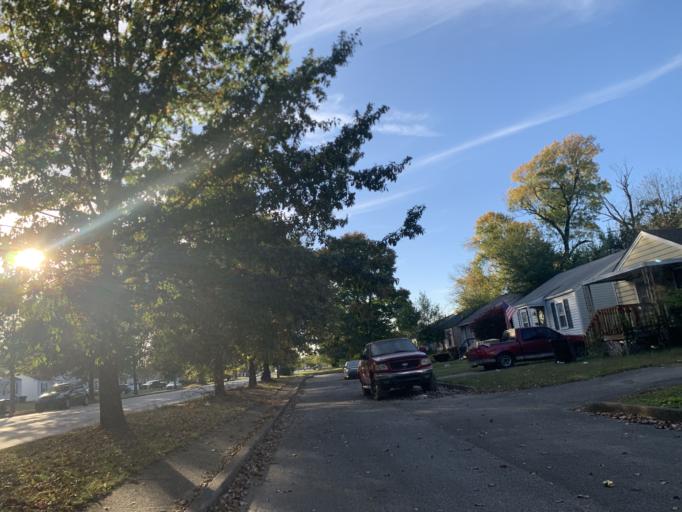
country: US
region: Kentucky
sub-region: Jefferson County
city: Shively
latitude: 38.2243
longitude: -85.8064
